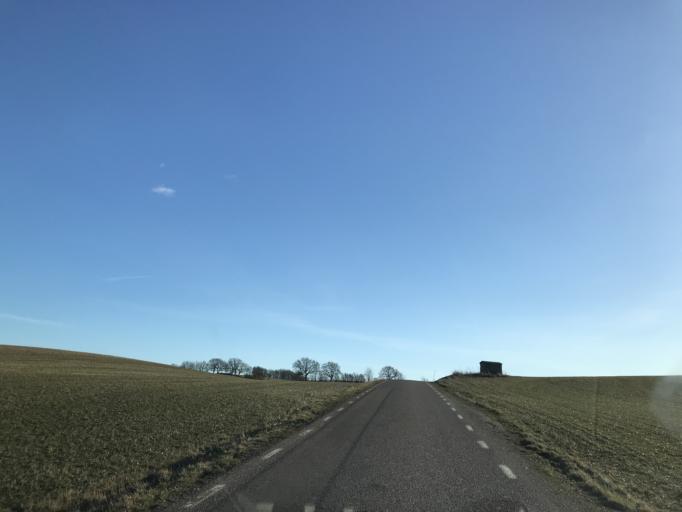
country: SE
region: Skane
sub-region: Ystads Kommun
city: Ystad
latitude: 55.5385
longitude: 13.7879
